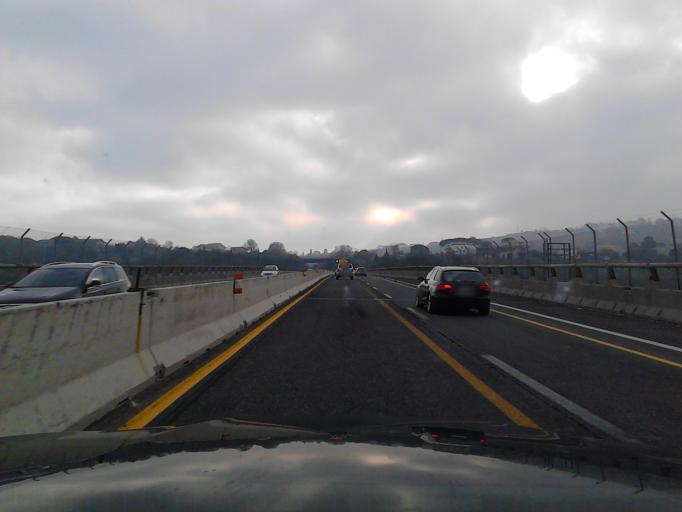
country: IT
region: Abruzzo
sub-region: Provincia di Teramo
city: Salino
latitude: 42.7748
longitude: 13.9314
